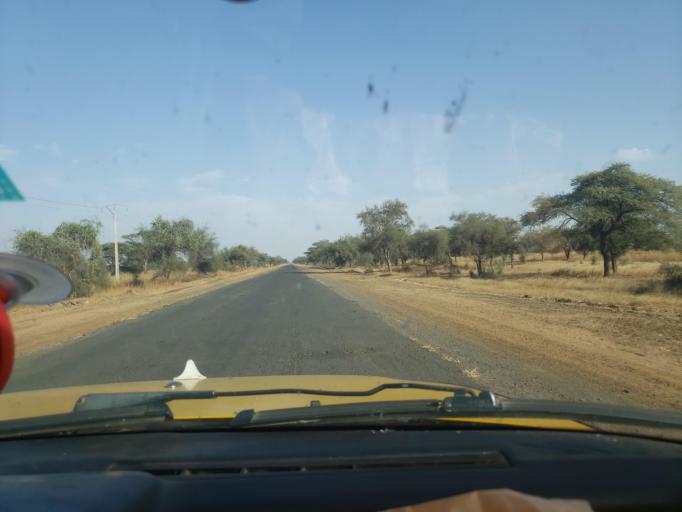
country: SN
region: Louga
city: Louga
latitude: 15.5070
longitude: -15.9670
